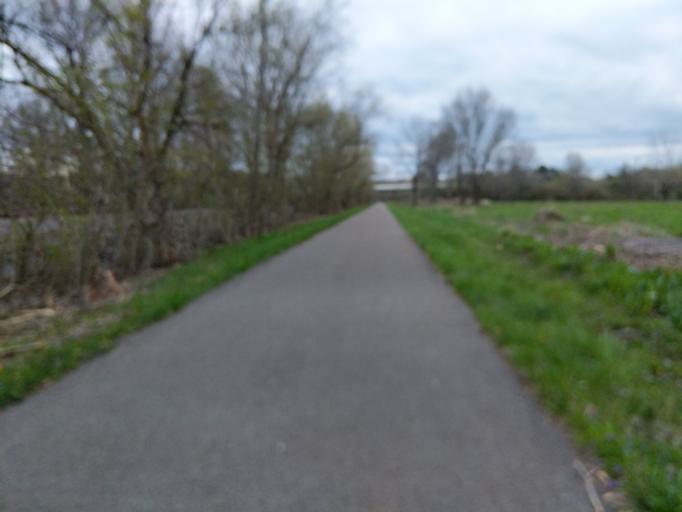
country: US
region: Ohio
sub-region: Athens County
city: The Plains
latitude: 39.3691
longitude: -82.1152
